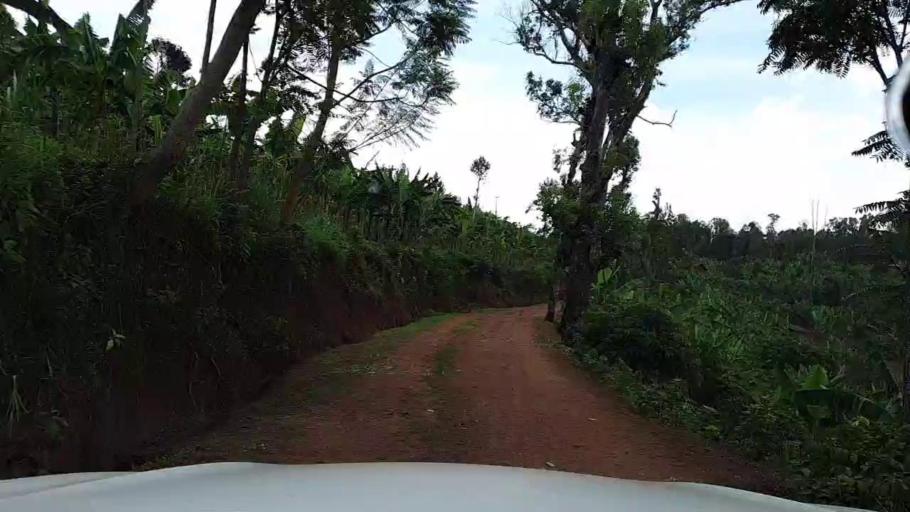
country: RW
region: Southern Province
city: Butare
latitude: -2.7517
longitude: 29.7618
